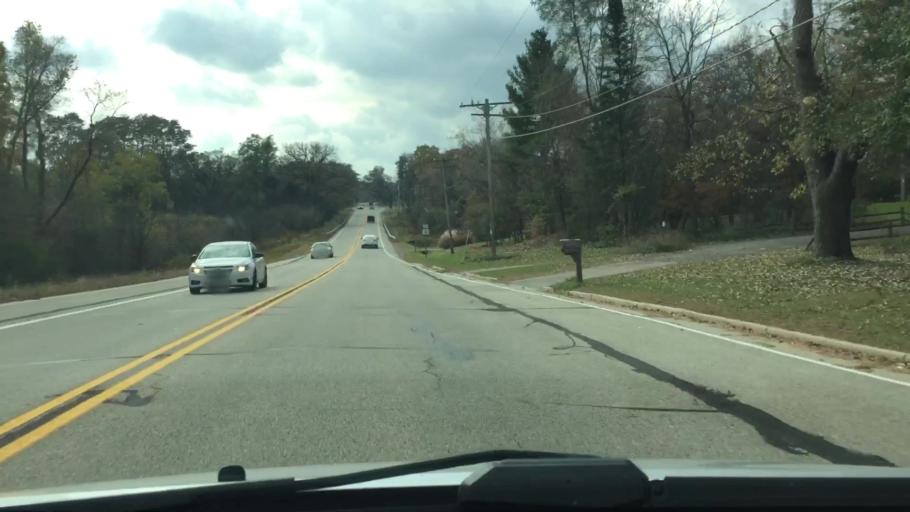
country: US
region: Wisconsin
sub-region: Waukesha County
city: Dousman
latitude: 42.9920
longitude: -88.4635
